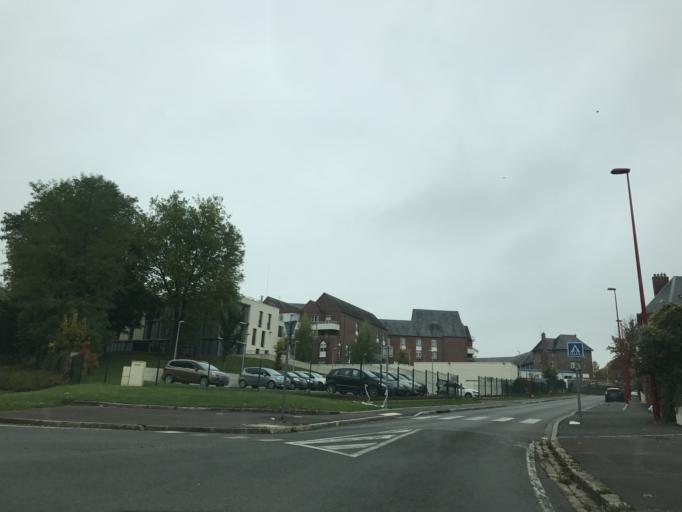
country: FR
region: Picardie
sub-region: Departement de la Somme
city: Peronne
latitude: 49.9328
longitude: 2.9306
